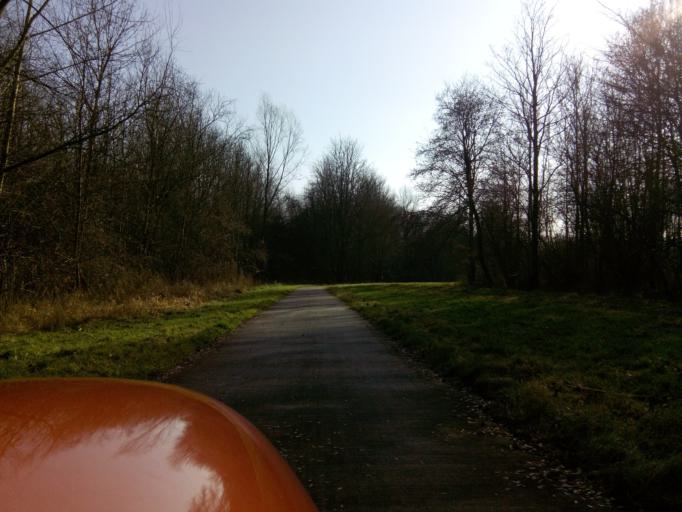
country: NL
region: Flevoland
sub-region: Gemeente Zeewolde
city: Zeewolde
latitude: 52.2996
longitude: 5.5025
